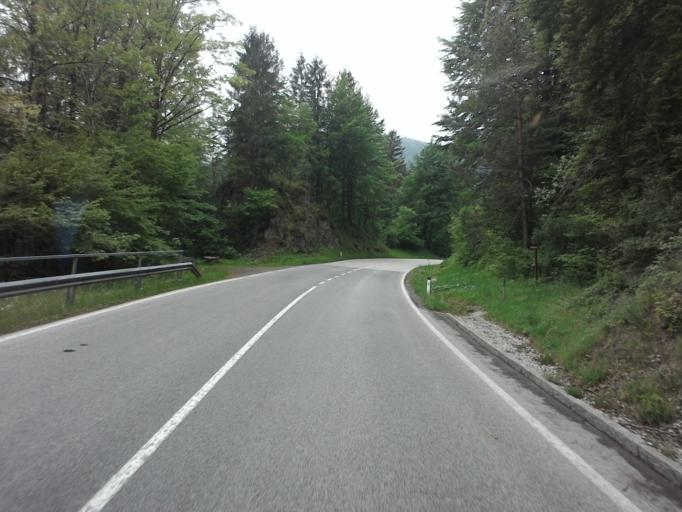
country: AT
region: Styria
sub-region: Politischer Bezirk Liezen
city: Landl
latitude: 47.6950
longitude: 14.6907
